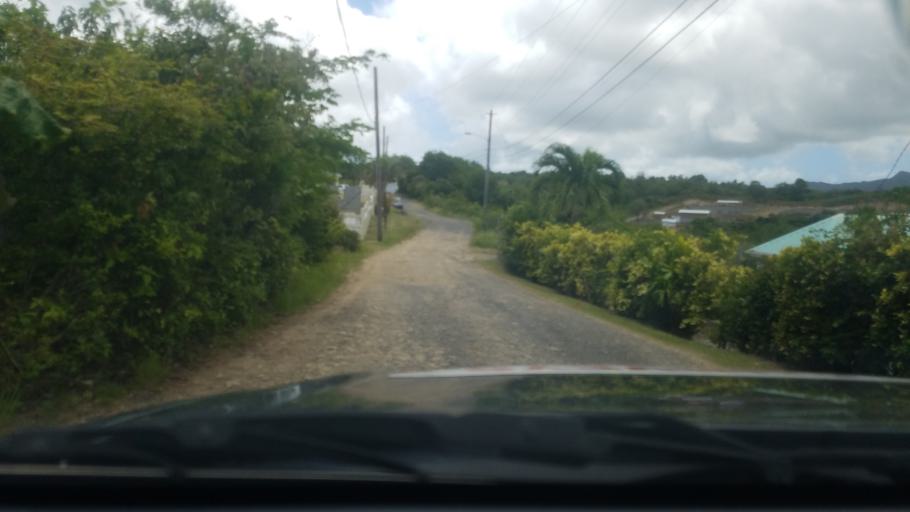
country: LC
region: Dennery Quarter
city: Dennery
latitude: 13.9192
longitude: -60.8966
